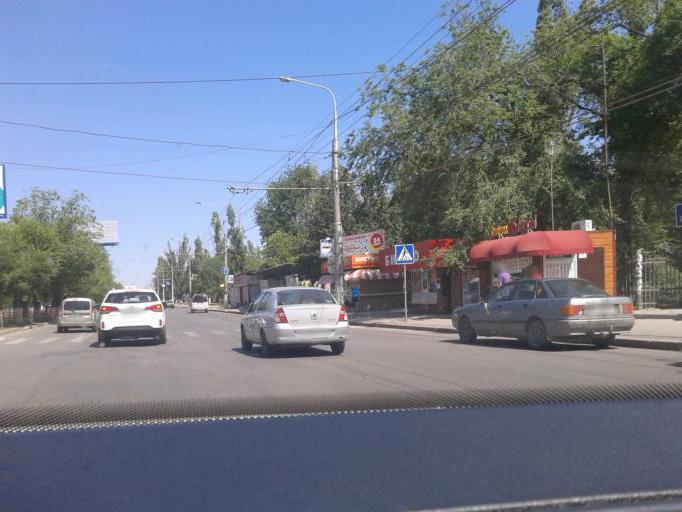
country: RU
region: Volgograd
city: Volgograd
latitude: 48.7356
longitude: 44.4944
